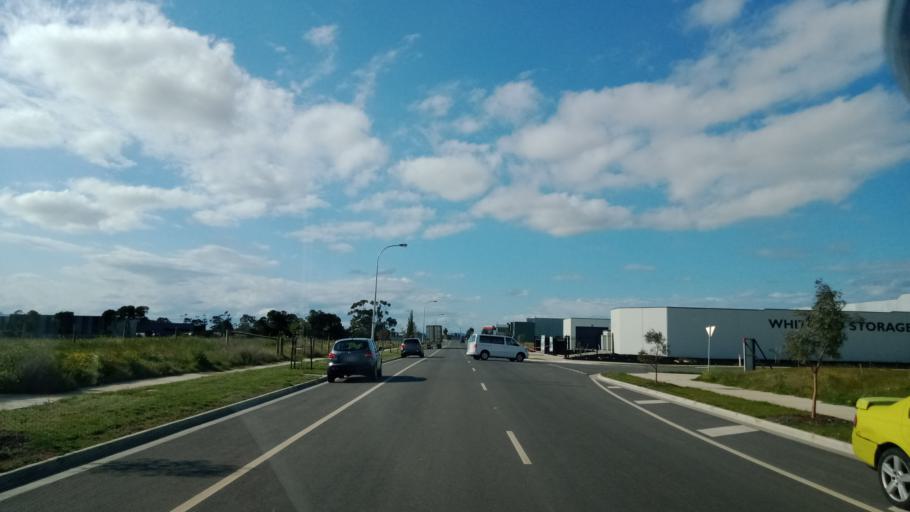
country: AU
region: Victoria
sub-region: Casey
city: Cranbourne West
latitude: -38.0839
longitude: 145.2427
